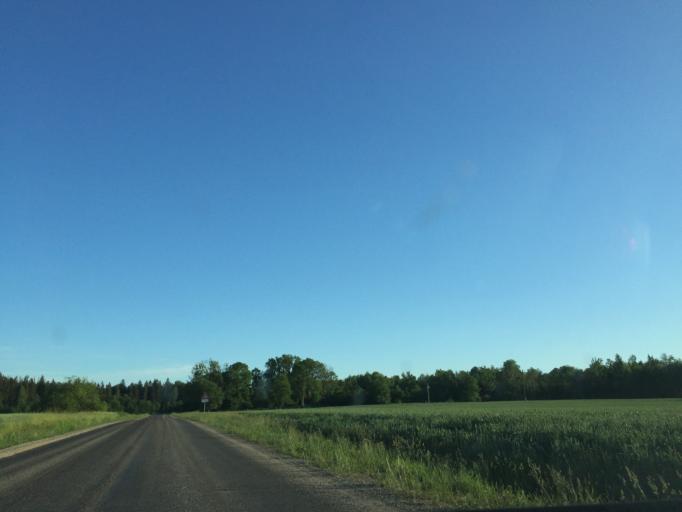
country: LV
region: Broceni
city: Broceni
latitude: 56.7372
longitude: 22.5085
